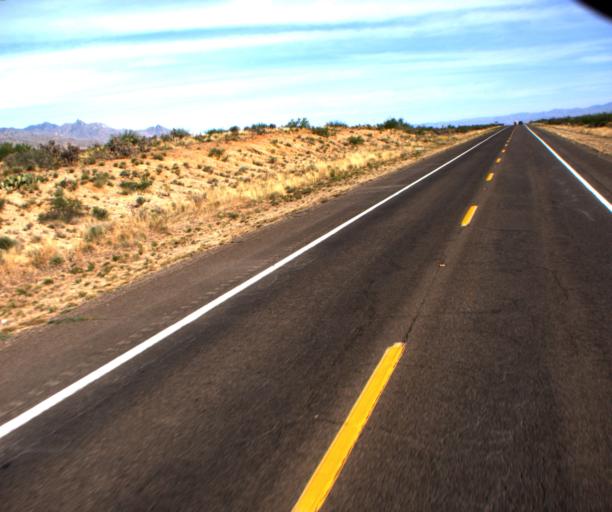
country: US
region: Arizona
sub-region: Graham County
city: Swift Trail Junction
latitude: 32.6184
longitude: -109.6886
